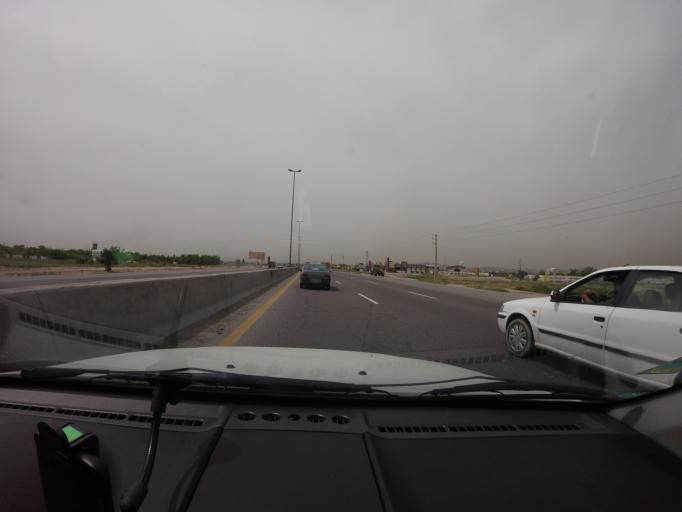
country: IR
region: Tehran
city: Robat Karim
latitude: 35.5233
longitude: 51.0823
